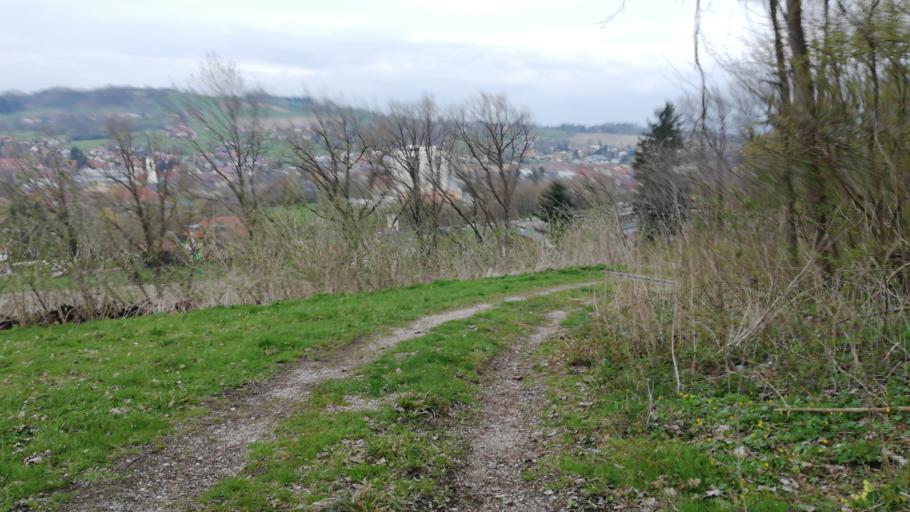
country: AT
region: Upper Austria
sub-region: Politischer Bezirk Grieskirchen
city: Bad Schallerbach
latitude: 48.2273
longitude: 13.9492
